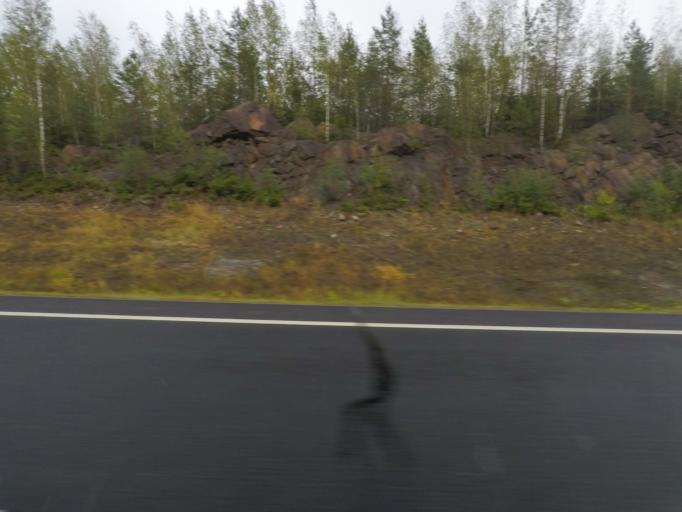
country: FI
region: Northern Savo
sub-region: Kuopio
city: Kuopio
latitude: 62.8227
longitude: 27.6107
